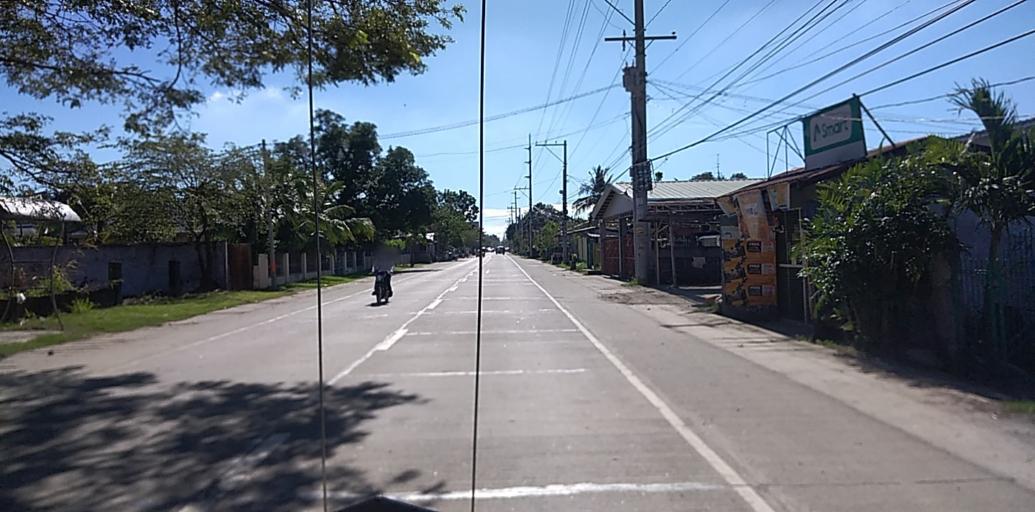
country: PH
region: Central Luzon
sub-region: Province of Pampanga
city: Santo Domingo
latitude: 15.0613
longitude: 120.7721
